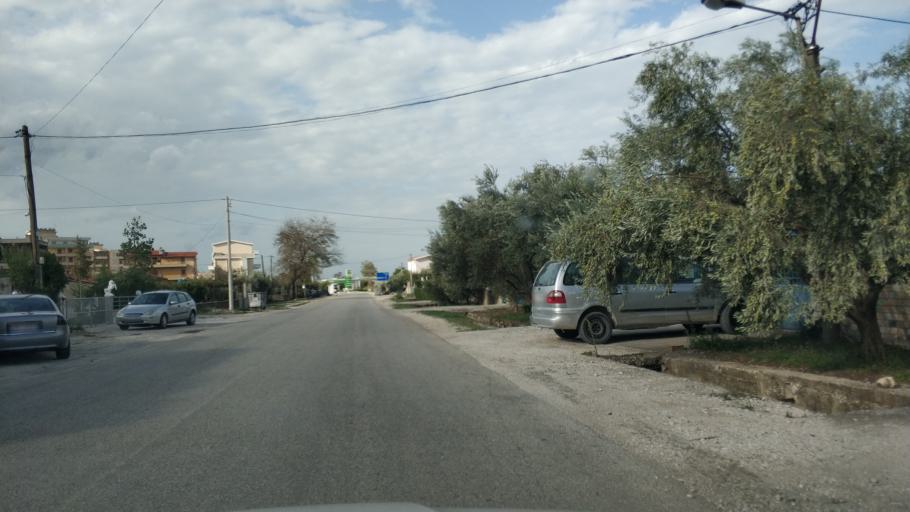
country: AL
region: Vlore
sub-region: Rrethi i Vlores
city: Orikum
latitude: 40.3271
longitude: 19.4787
